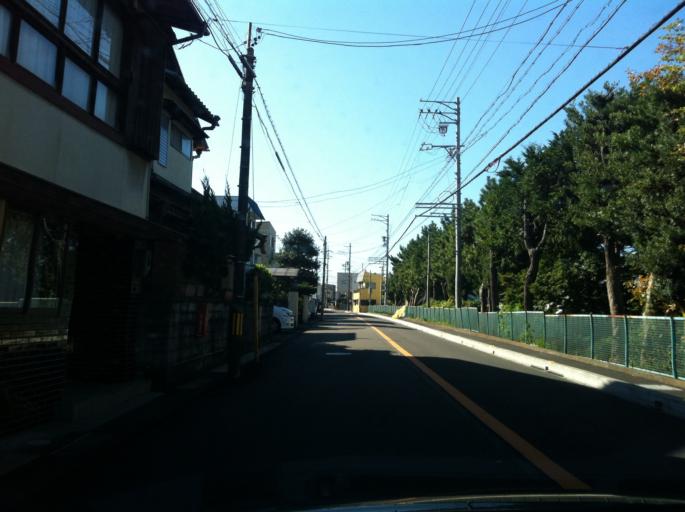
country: JP
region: Shizuoka
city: Shizuoka-shi
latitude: 35.0074
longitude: 138.4543
